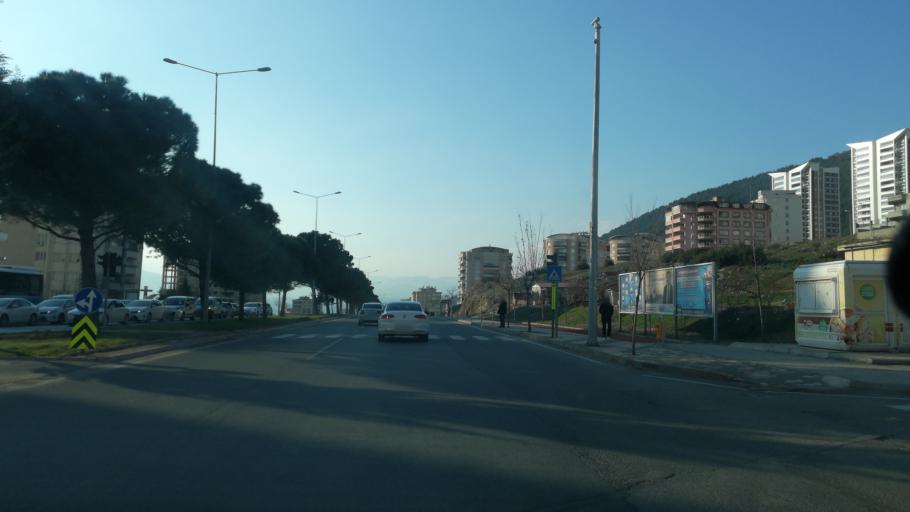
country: TR
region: Kahramanmaras
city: Kahramanmaras
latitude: 37.5958
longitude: 36.8514
